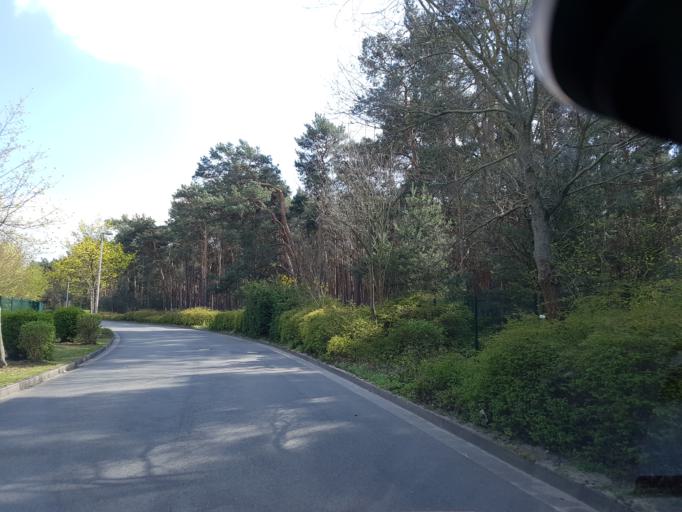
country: DE
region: Brandenburg
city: Linthe
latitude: 52.1663
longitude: 12.7759
